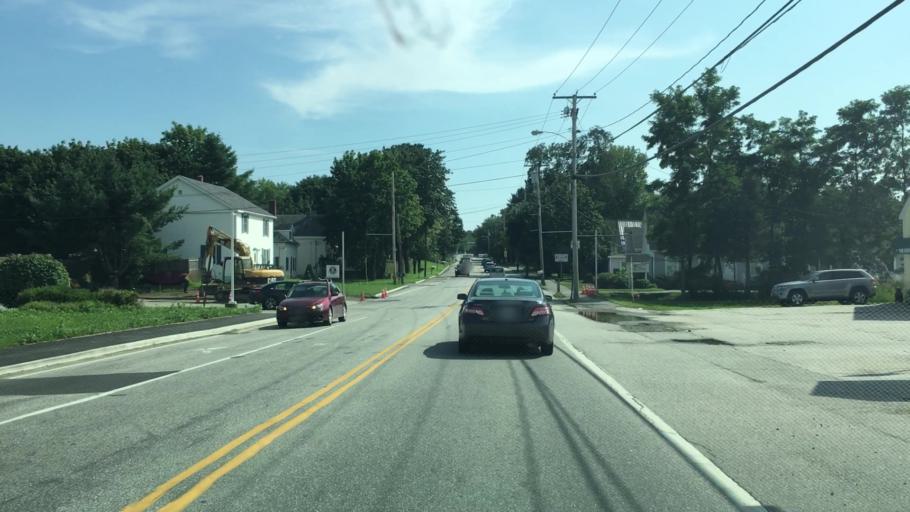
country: US
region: Maine
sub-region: Penobscot County
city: Hampden
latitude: 44.7443
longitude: -68.8378
